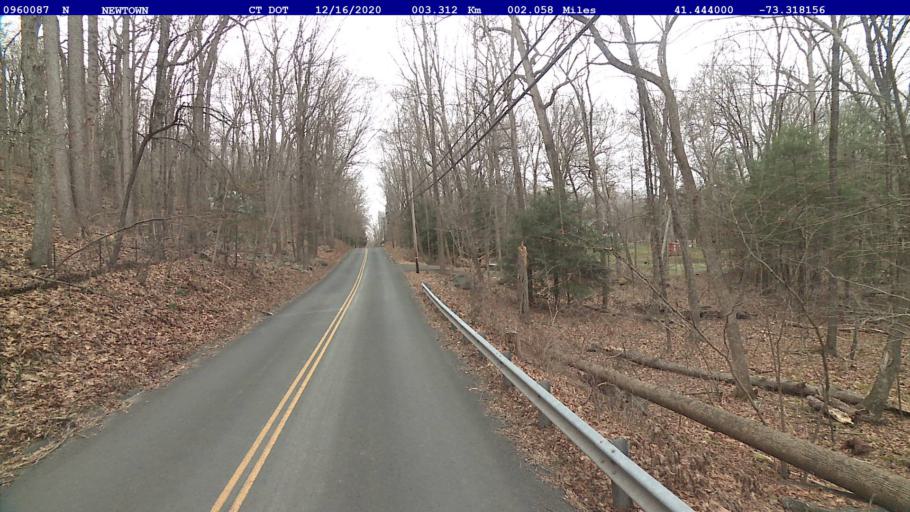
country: US
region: Connecticut
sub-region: Fairfield County
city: Newtown
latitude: 41.4442
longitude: -73.3181
